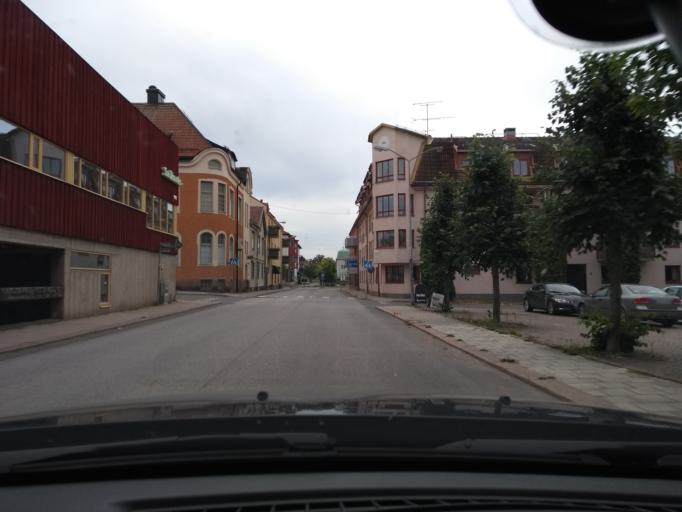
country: SE
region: Joenkoeping
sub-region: Eksjo Kommun
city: Eksjoe
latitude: 57.6659
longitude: 14.9702
